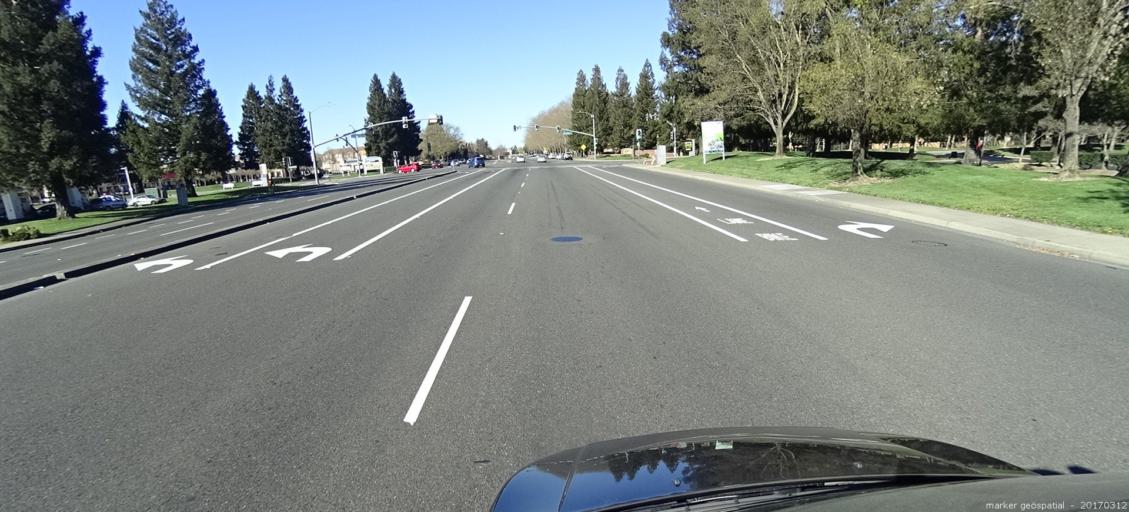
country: US
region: California
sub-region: Yolo County
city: West Sacramento
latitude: 38.6146
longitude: -121.5161
